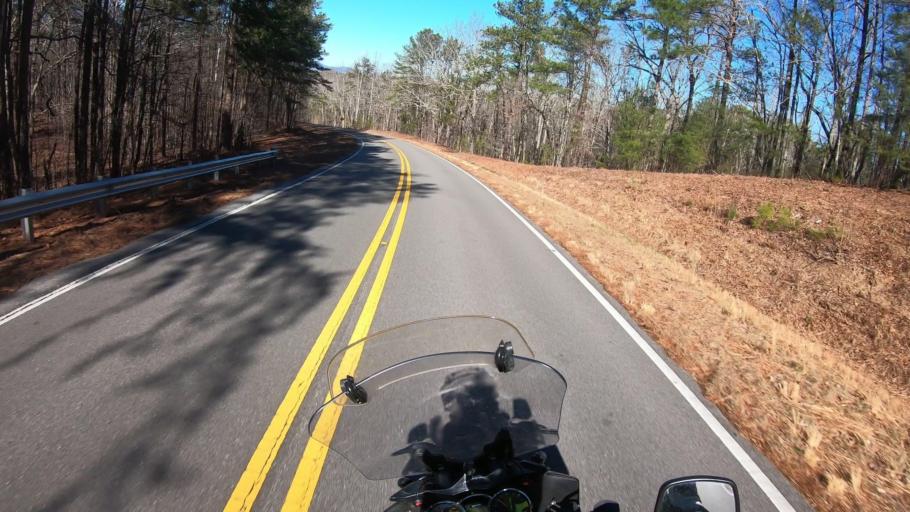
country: US
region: Alabama
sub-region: Calhoun County
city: Choccolocco
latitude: 33.5641
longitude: -85.6982
